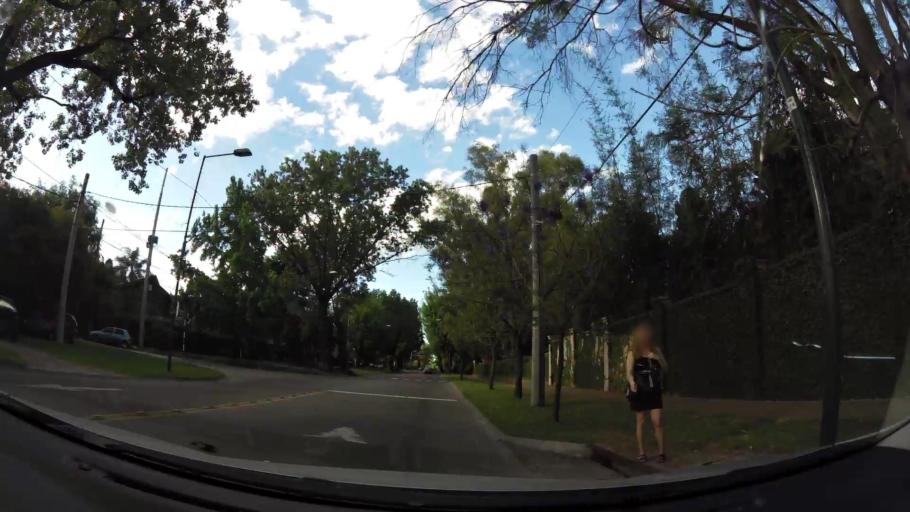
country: AR
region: Buenos Aires
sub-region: Partido de San Isidro
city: San Isidro
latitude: -34.4870
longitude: -58.5565
